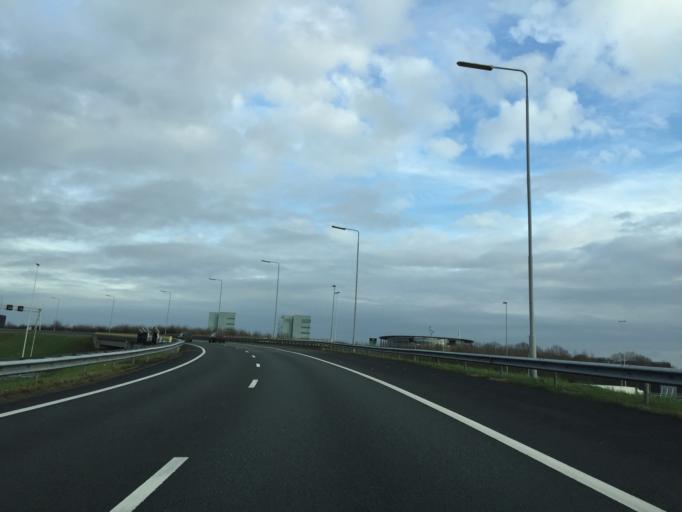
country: NL
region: Utrecht
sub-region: Gemeente Nieuwegein
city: Nieuwegein
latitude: 52.0639
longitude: 5.0725
